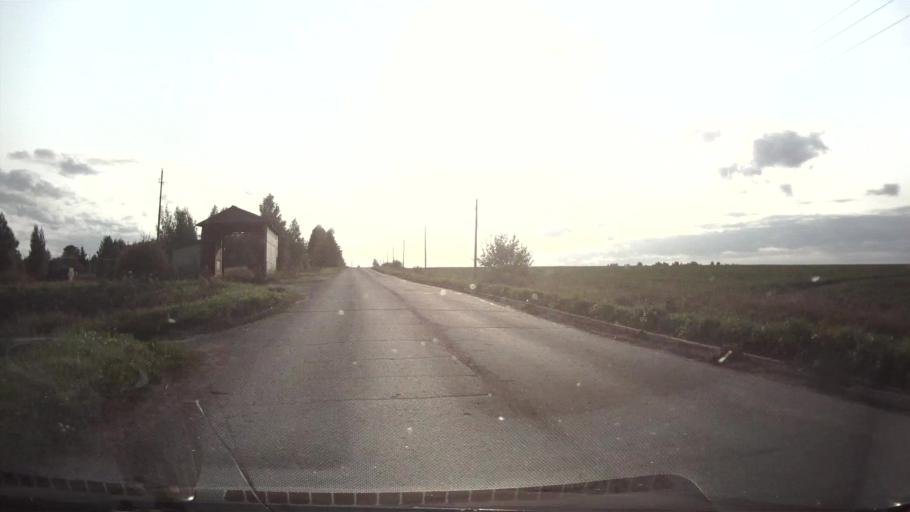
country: RU
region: Mariy-El
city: Kuzhener
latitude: 56.9627
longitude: 48.7811
